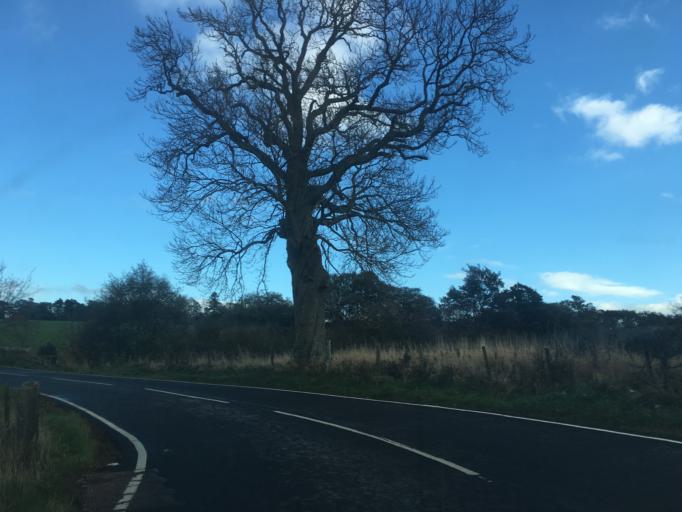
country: GB
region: Scotland
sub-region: East Lothian
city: Pencaitland
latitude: 55.8428
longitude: -2.8783
